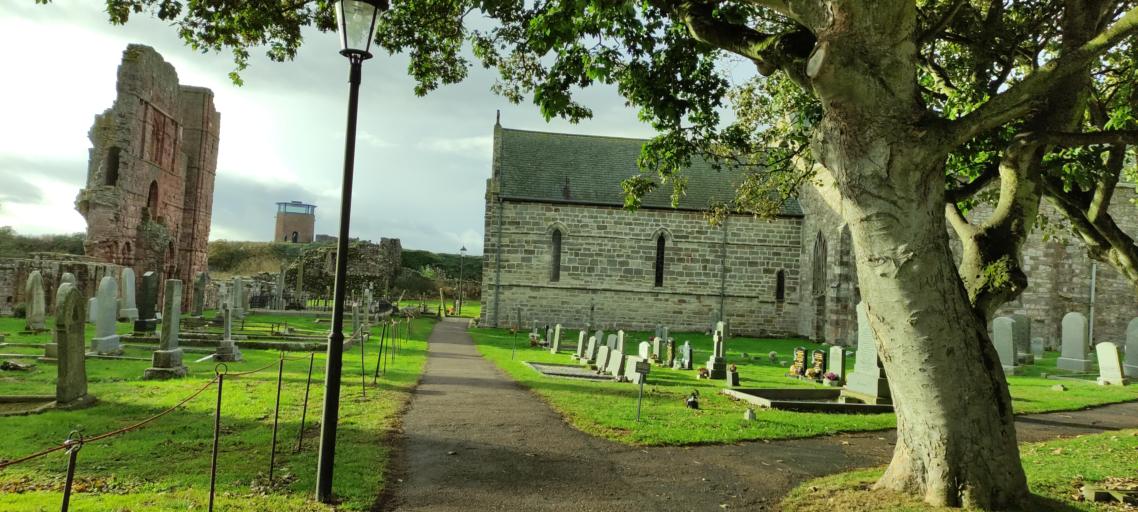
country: GB
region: England
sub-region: Northumberland
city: Belford
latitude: 55.6698
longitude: -1.8015
